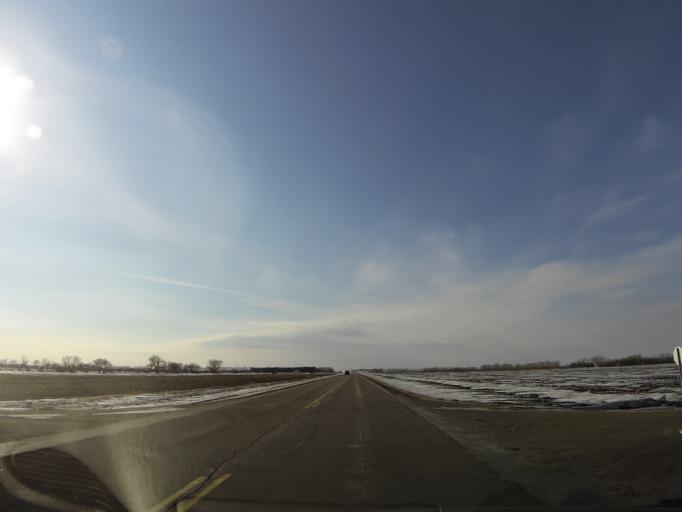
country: US
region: North Dakota
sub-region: Walsh County
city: Grafton
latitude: 48.4122
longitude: -97.1682
